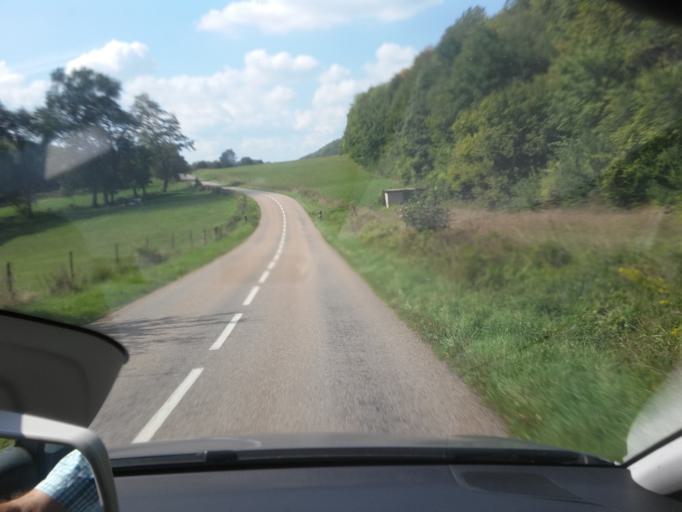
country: BE
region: Wallonia
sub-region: Province du Luxembourg
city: Rouvroy
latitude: 49.4965
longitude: 5.5412
